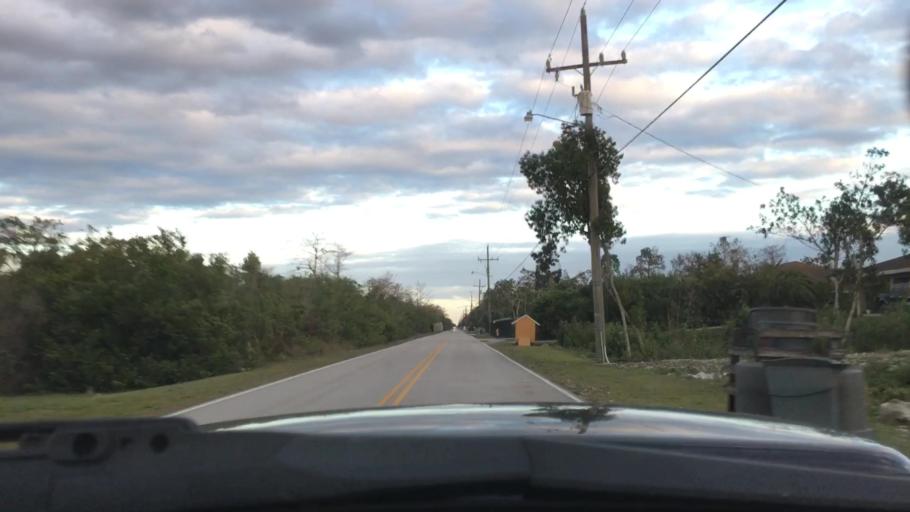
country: US
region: Florida
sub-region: Miami-Dade County
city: Kendall West
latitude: 25.7607
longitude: -80.8510
